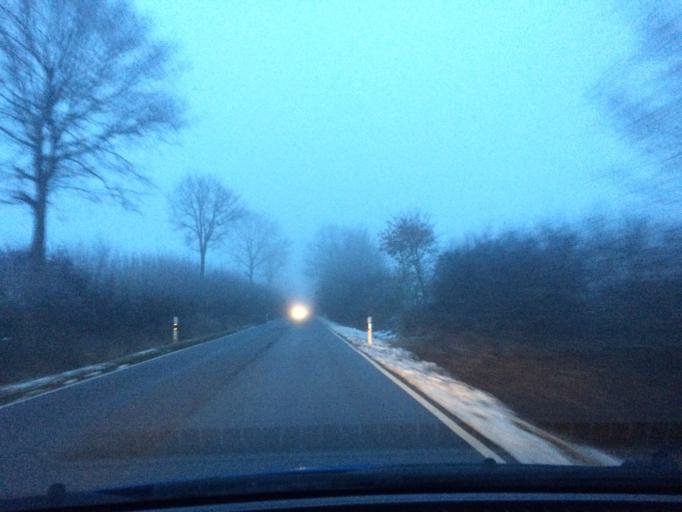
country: DE
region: Schleswig-Holstein
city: Kollow
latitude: 53.4562
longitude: 10.4593
